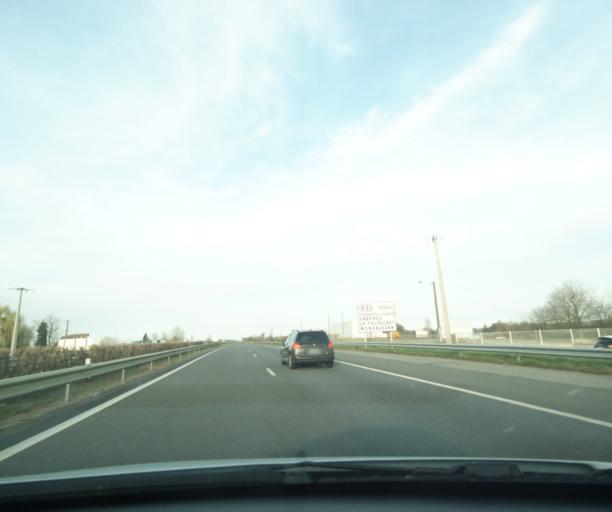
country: FR
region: Midi-Pyrenees
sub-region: Departement de la Haute-Garonne
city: Cazeres
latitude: 43.2297
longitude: 1.0629
